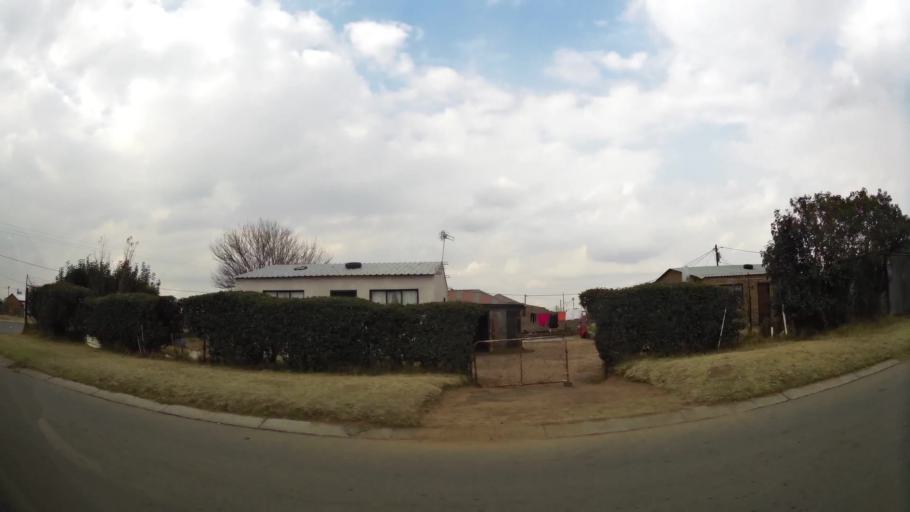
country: ZA
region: Orange Free State
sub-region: Fezile Dabi District Municipality
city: Sasolburg
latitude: -26.8482
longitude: 27.8782
